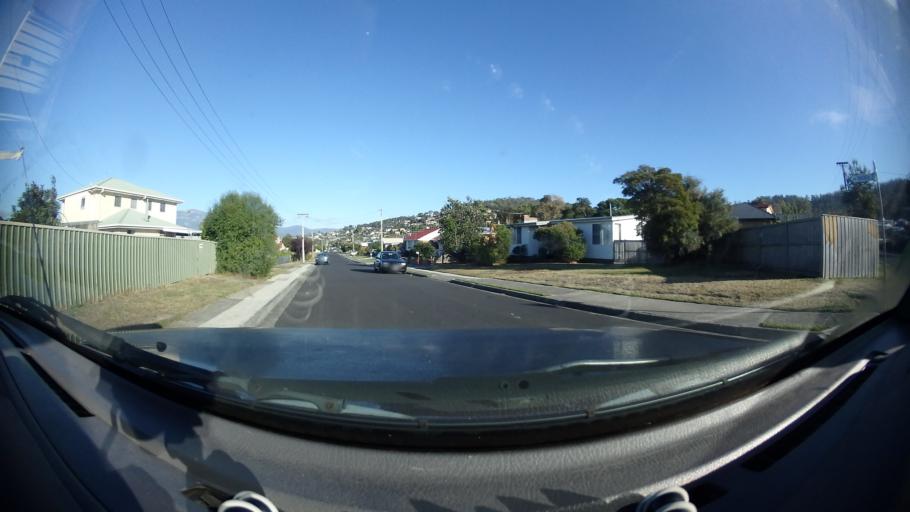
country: AU
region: Tasmania
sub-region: Clarence
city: Howrah
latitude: -42.8758
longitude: 147.3983
